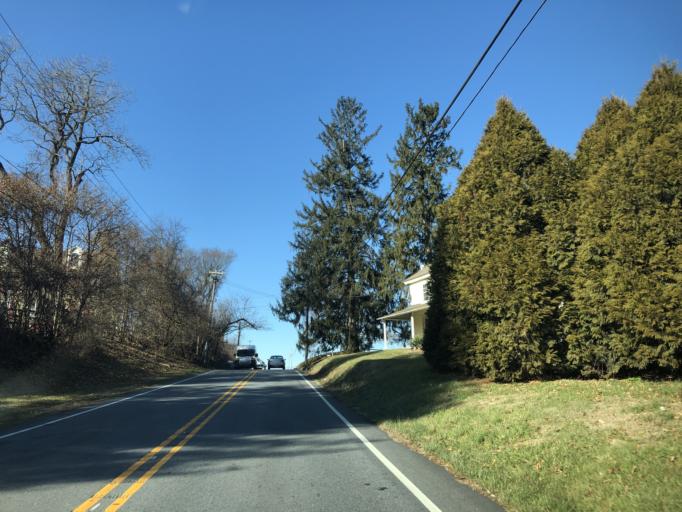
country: US
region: Pennsylvania
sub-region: Chester County
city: Upland
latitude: 39.9076
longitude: -75.8001
